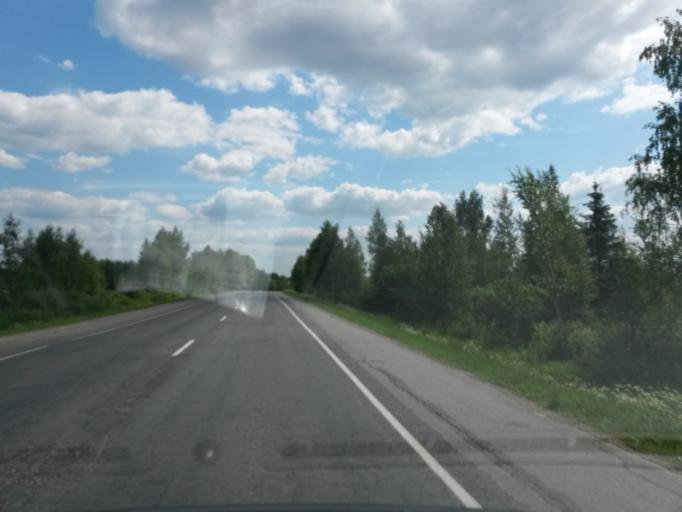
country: RU
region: Jaroslavl
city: Yaroslavl
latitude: 57.5559
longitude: 39.8707
